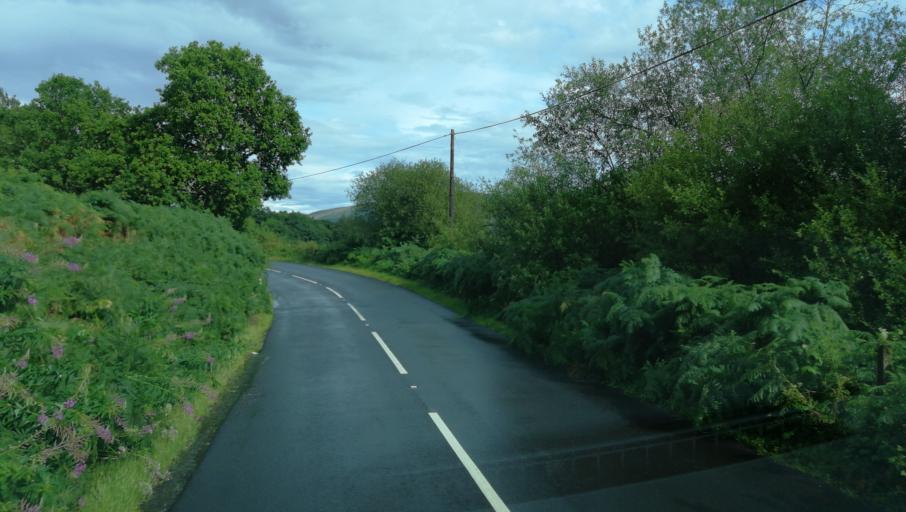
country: GB
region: Scotland
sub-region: Stirling
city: Callander
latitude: 56.2270
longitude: -4.3345
